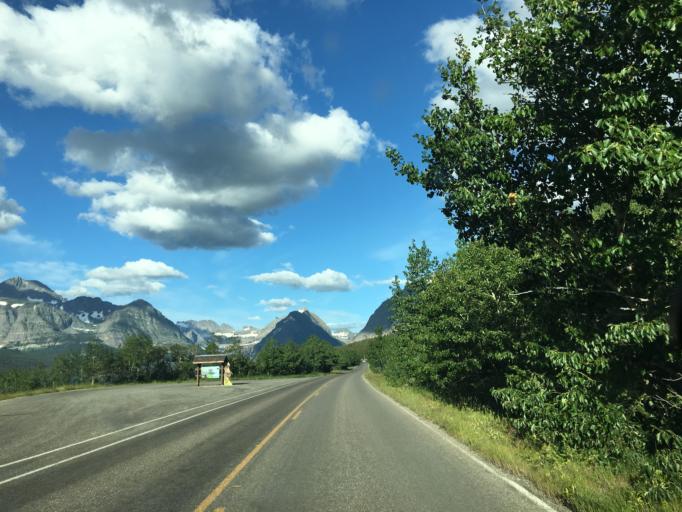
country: CA
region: Alberta
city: Cardston
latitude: 48.8244
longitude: -113.5700
